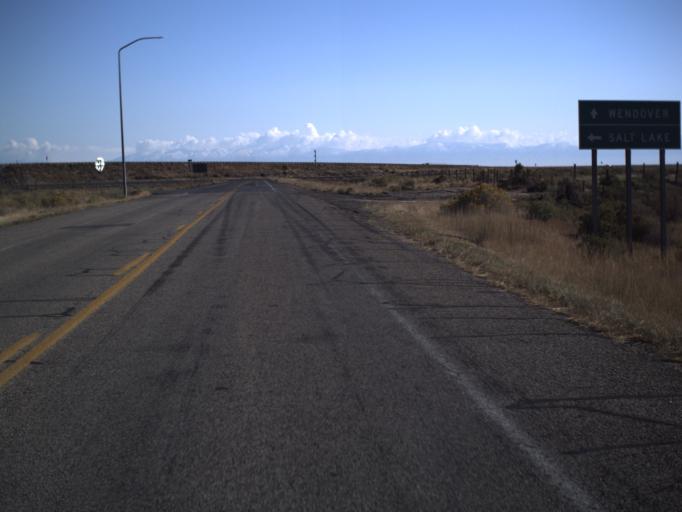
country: US
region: Utah
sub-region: Tooele County
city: Grantsville
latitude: 40.6796
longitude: -112.4443
